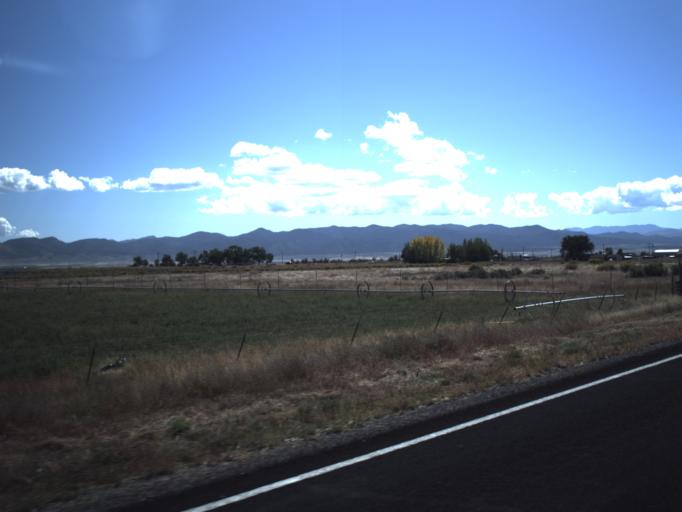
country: US
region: Utah
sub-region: Washington County
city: Enterprise
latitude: 37.6983
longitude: -113.6565
